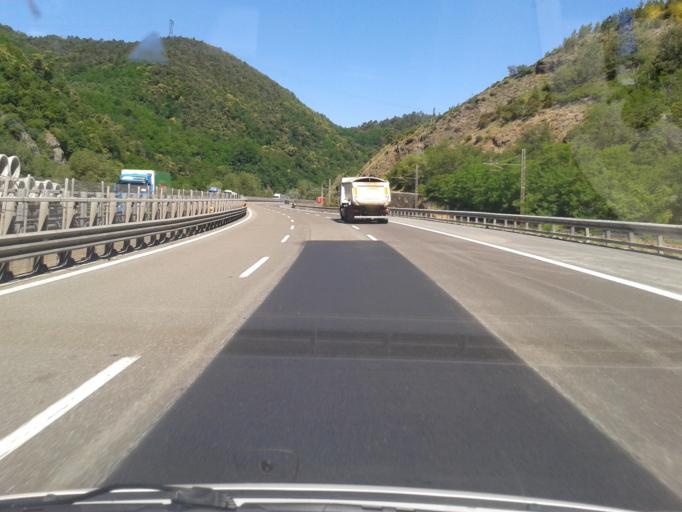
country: IT
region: Piedmont
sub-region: Provincia di Alessandria
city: Belforte Monferrato
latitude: 44.6010
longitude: 8.6662
